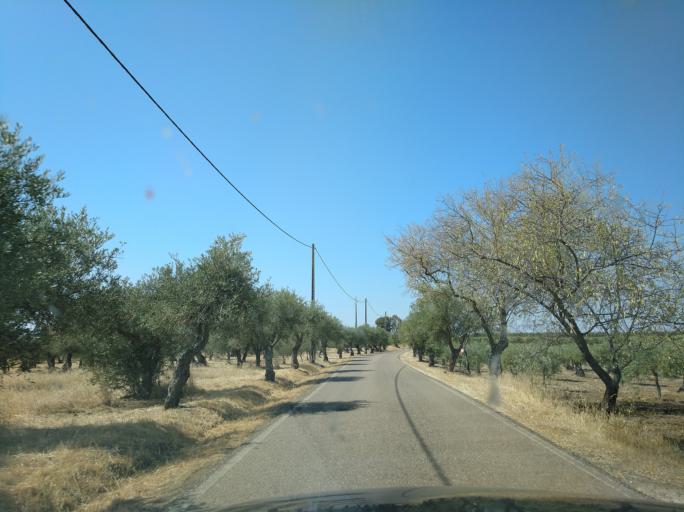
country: PT
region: Portalegre
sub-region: Campo Maior
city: Campo Maior
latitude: 39.0323
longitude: -7.0436
